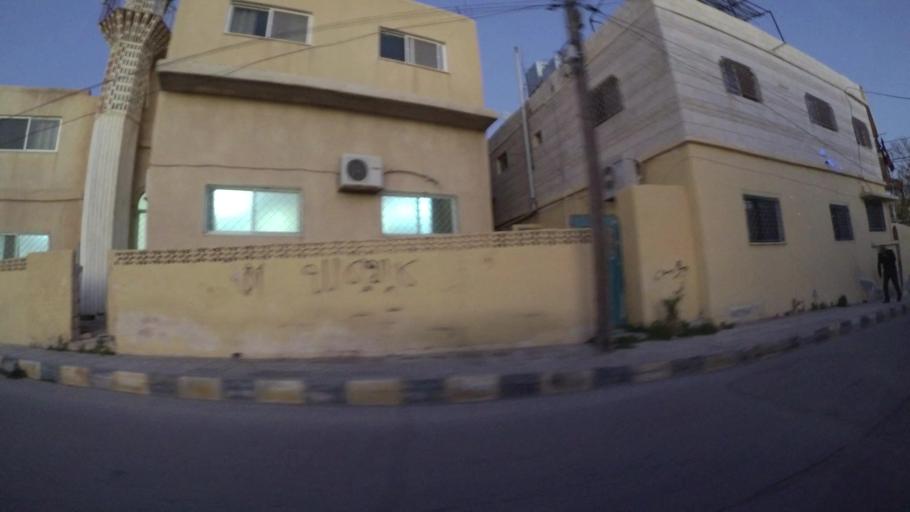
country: JO
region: Ma'an
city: Petra
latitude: 30.3253
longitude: 35.4770
